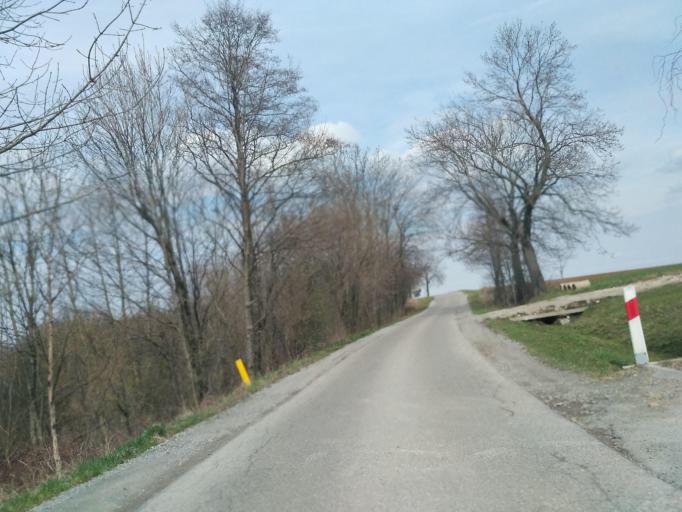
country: PL
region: Subcarpathian Voivodeship
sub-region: Powiat ropczycko-sedziszowski
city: Sedziszow Malopolski
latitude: 50.0491
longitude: 21.7168
